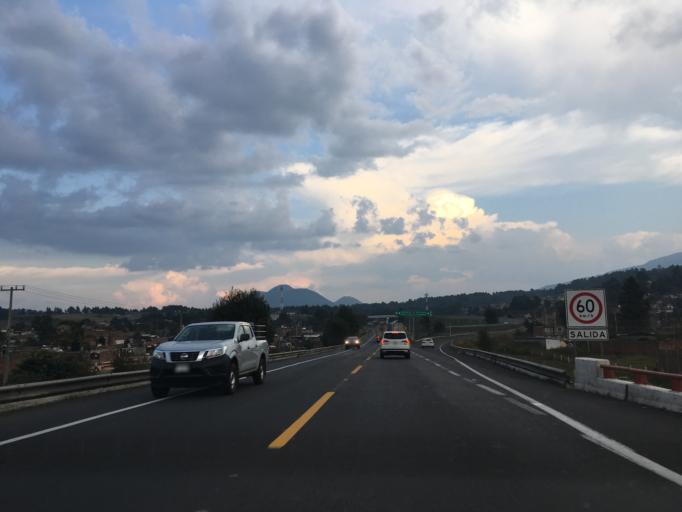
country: MX
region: Michoacan
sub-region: Patzcuaro
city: Colonia Vista Bella (Lomas del Peaje)
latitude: 19.4931
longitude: -101.6058
